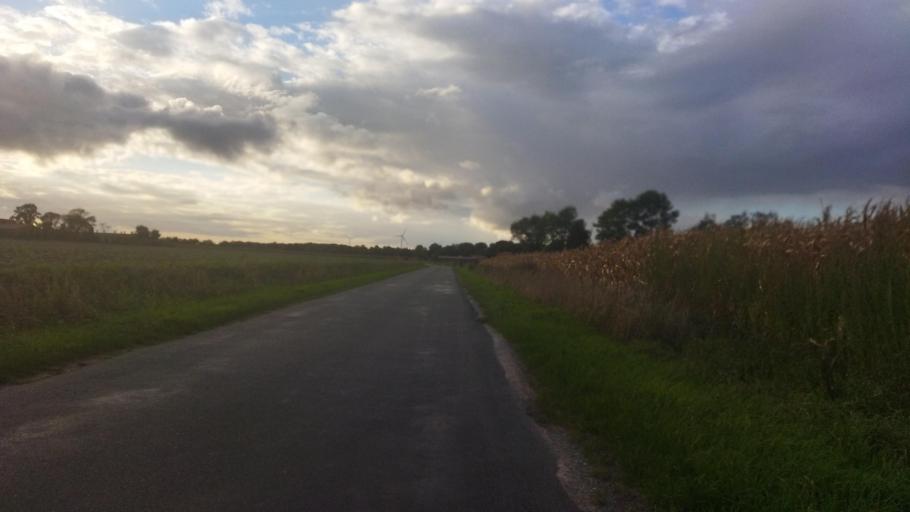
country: DE
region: North Rhine-Westphalia
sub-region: Regierungsbezirk Munster
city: Billerbeck
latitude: 51.9789
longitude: 7.2351
